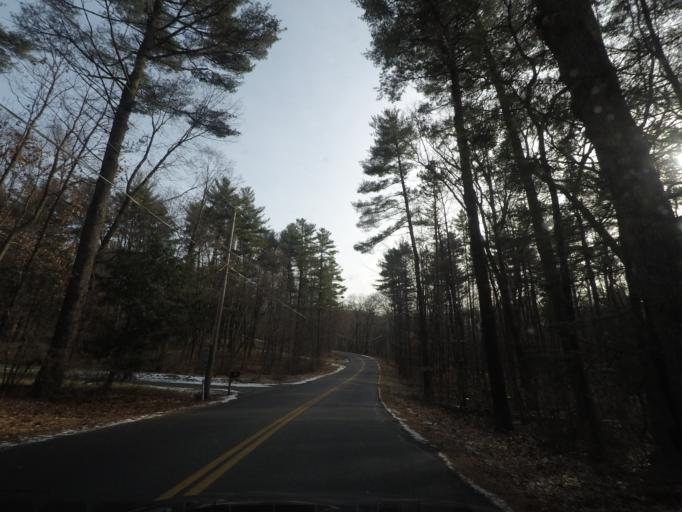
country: US
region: New York
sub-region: Saratoga County
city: Stillwater
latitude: 42.9908
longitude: -73.7249
